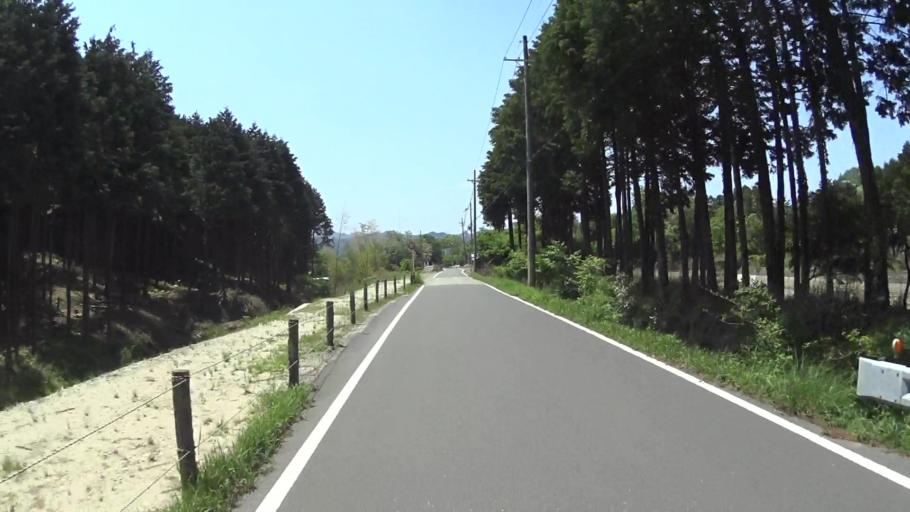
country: JP
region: Kyoto
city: Kameoka
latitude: 35.0853
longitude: 135.5675
